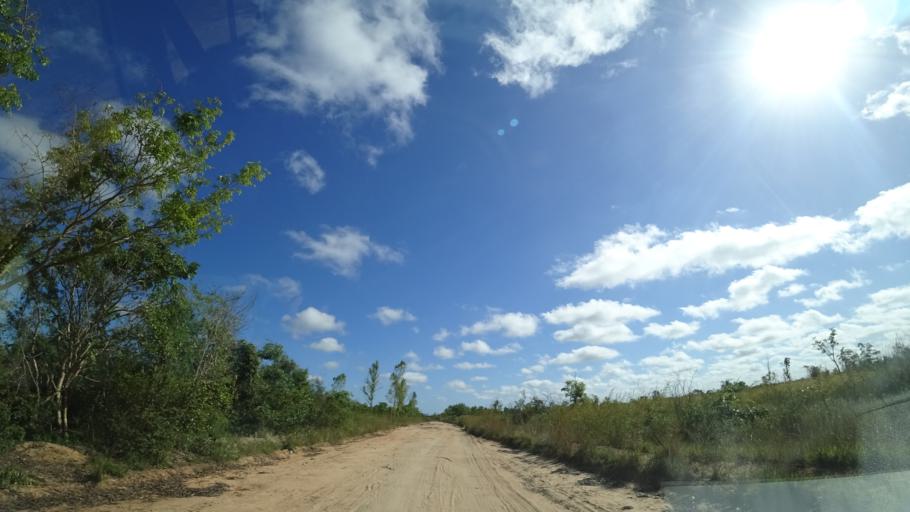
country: MZ
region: Sofala
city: Dondo
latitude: -19.4408
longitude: 34.7147
